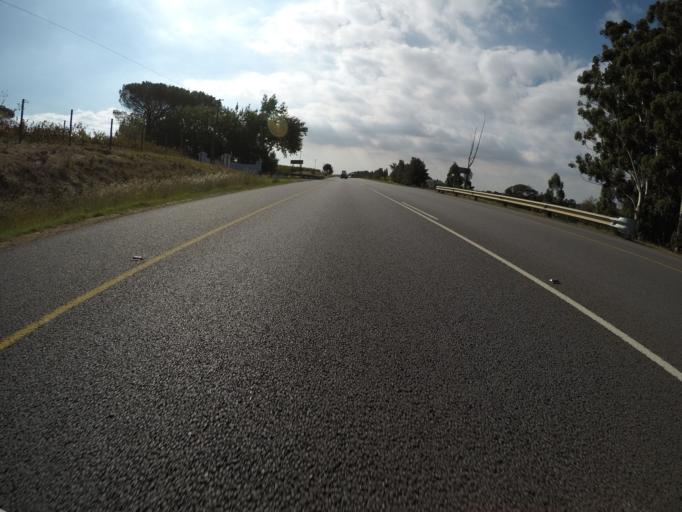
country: ZA
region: Western Cape
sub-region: Cape Winelands District Municipality
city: Stellenbosch
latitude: -33.8835
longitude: 18.8196
